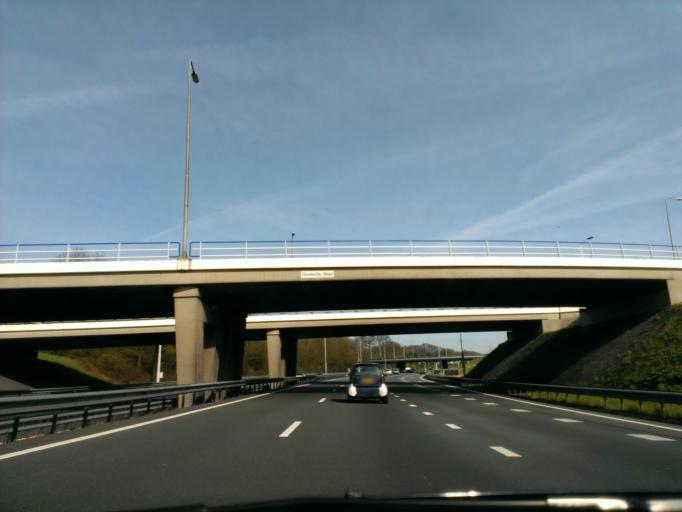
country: NL
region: North Holland
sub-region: Gemeente Bussum
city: Bussum
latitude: 52.2780
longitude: 5.1855
